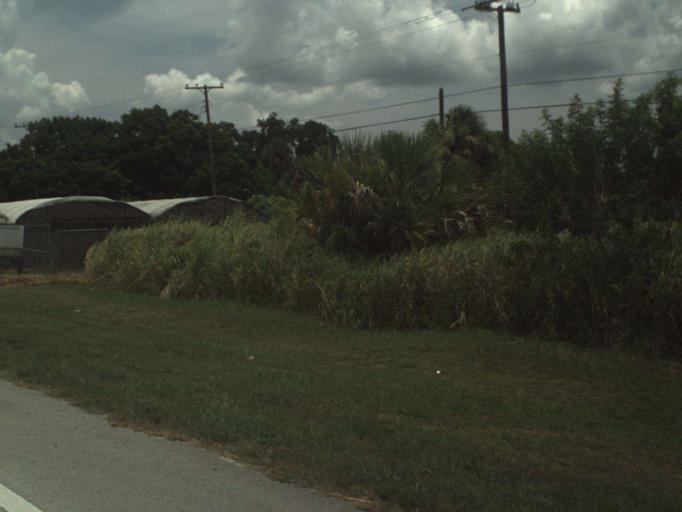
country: US
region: Florida
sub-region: Saint Lucie County
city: Lakewood Park
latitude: 27.5042
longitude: -80.3985
